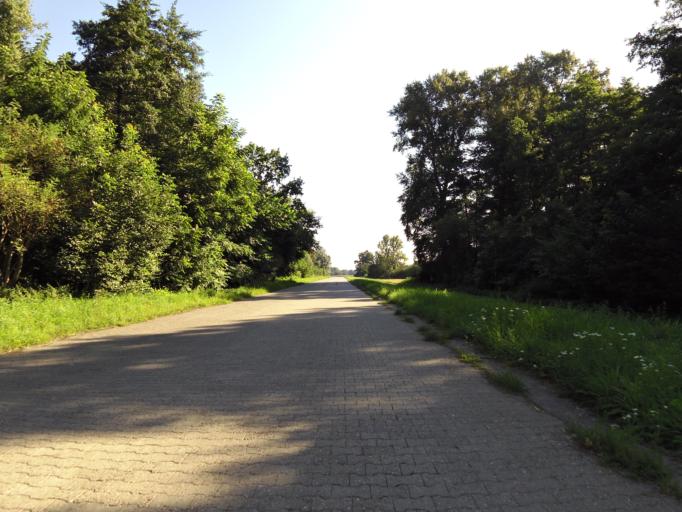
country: DE
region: Hesse
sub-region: Regierungsbezirk Darmstadt
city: Gross-Rohrheim
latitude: 49.7401
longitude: 8.4682
